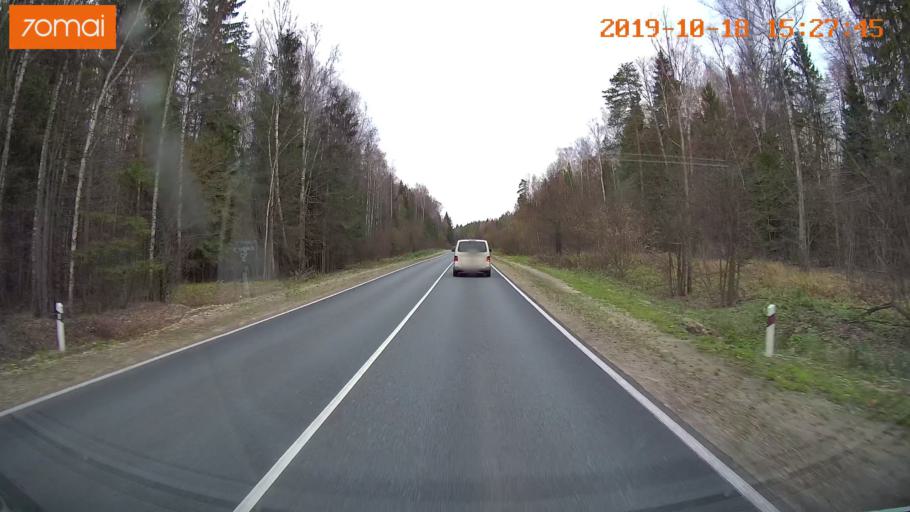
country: RU
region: Vladimir
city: Anopino
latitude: 55.7574
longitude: 40.6722
